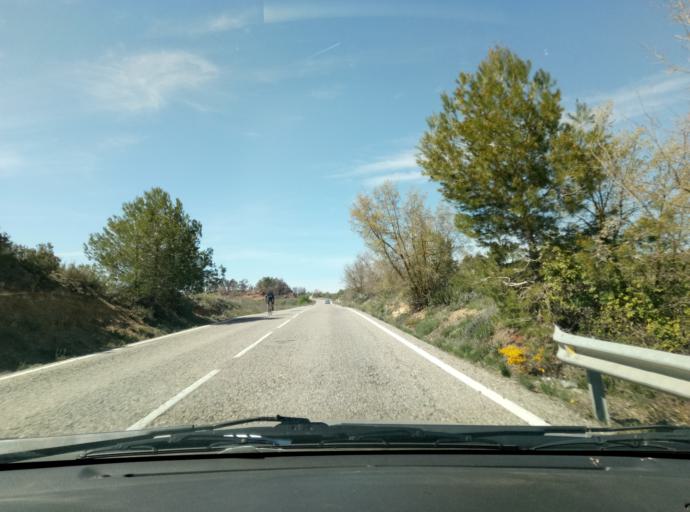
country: ES
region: Catalonia
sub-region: Provincia de Lleida
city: Vinaixa
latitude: 41.4317
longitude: 0.9591
